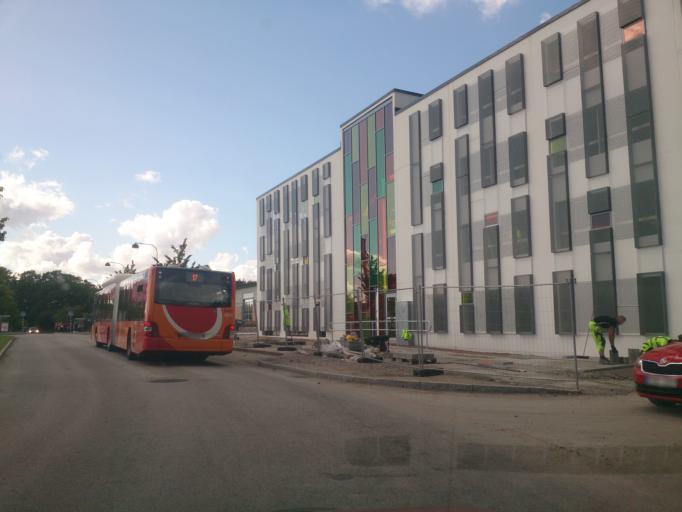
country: SE
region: OEstergoetland
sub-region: Linkopings Kommun
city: Linkoping
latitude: 58.3915
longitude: 15.6270
